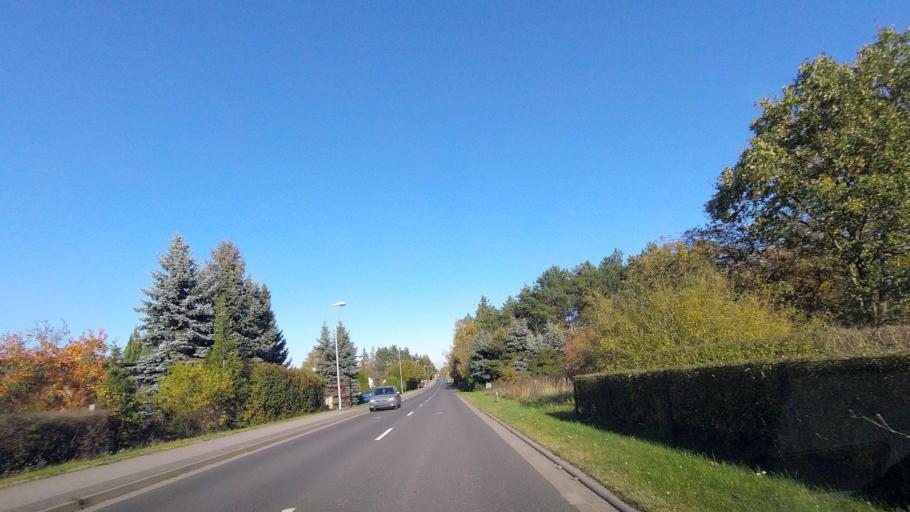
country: DE
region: Saxony-Anhalt
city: Zahna
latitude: 51.9098
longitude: 12.7758
